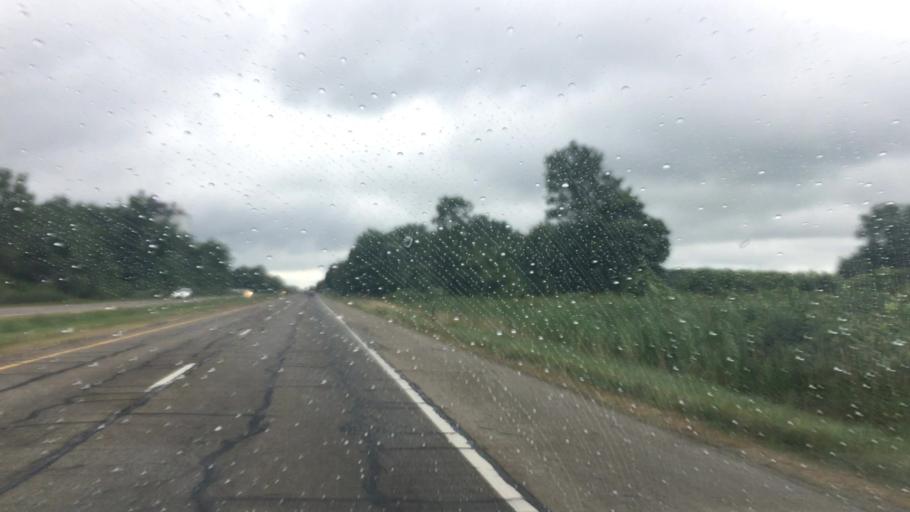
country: US
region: Michigan
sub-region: Ottawa County
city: Beechwood
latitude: 42.8654
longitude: -86.1103
